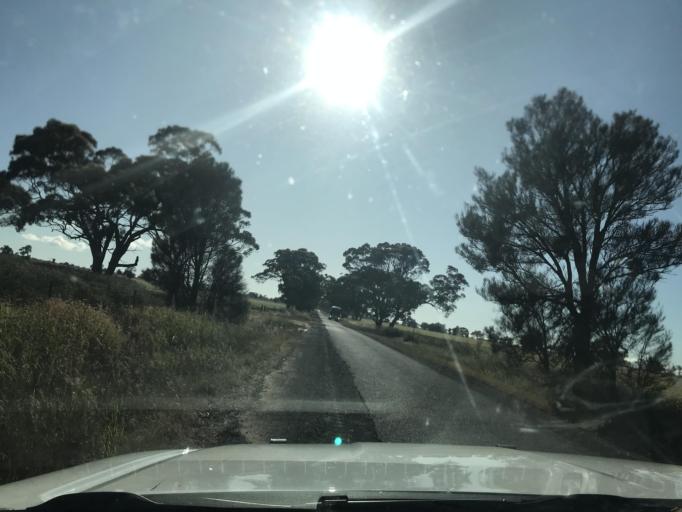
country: AU
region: Victoria
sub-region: Horsham
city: Horsham
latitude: -36.6915
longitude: 141.5386
